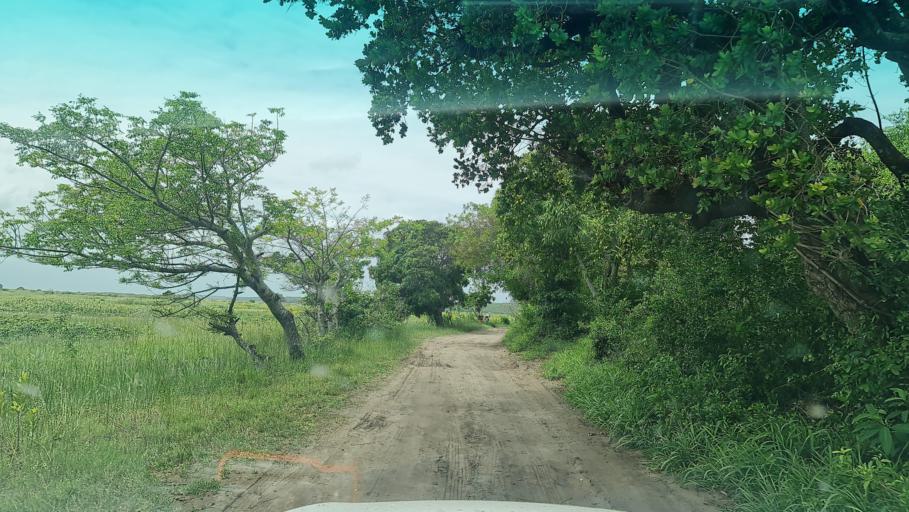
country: MZ
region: Maputo
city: Manhica
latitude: -25.5229
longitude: 32.8611
